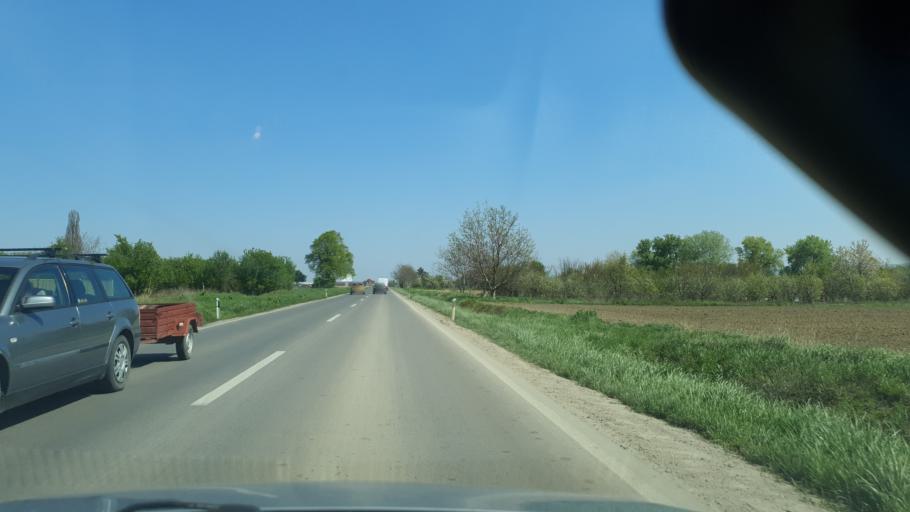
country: RS
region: Autonomna Pokrajina Vojvodina
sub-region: Juznobacki Okrug
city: Beocin
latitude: 45.2417
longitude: 19.6555
